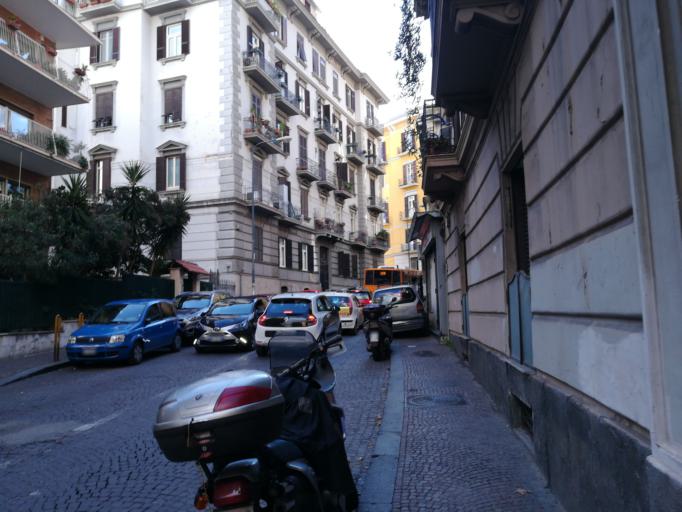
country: IT
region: Campania
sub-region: Provincia di Napoli
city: Napoli
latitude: 40.8385
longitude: 14.2369
